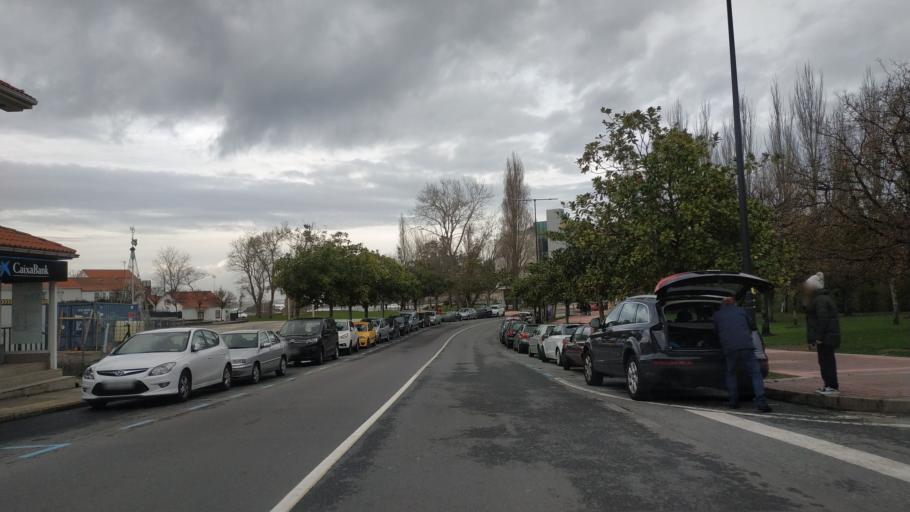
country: ES
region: Galicia
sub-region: Provincia da Coruna
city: Oleiros
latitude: 43.3473
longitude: -8.3459
